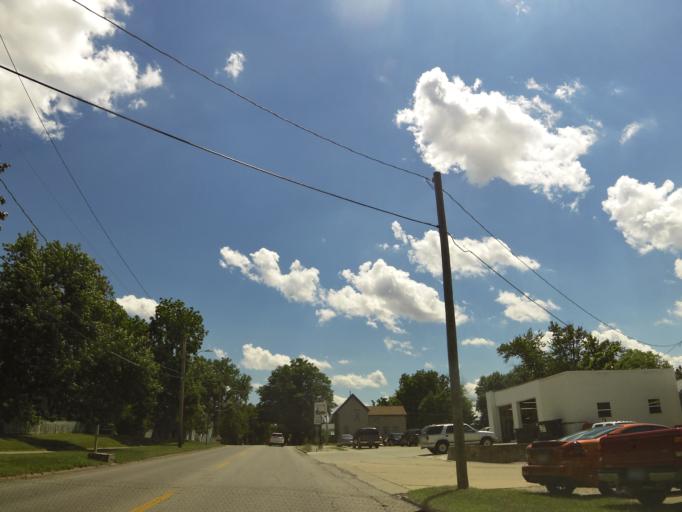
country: US
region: Iowa
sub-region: Buchanan County
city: Independence
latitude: 42.4765
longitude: -91.8894
